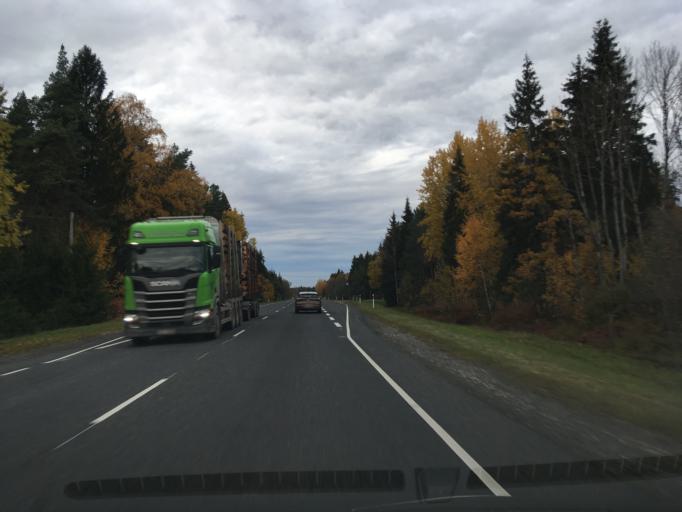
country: EE
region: Harju
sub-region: Nissi vald
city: Turba
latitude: 58.9331
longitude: 24.0980
